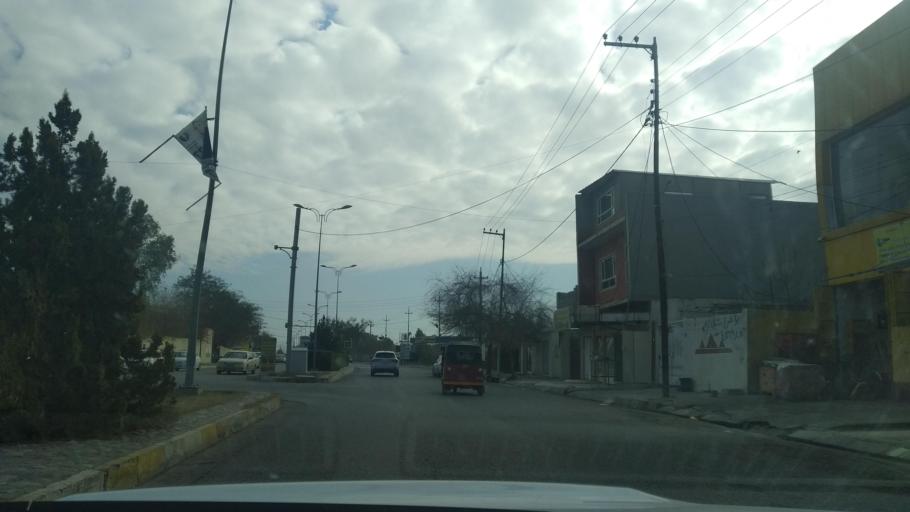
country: IQ
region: Arbil
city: Erbil
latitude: 36.1759
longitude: 44.0319
